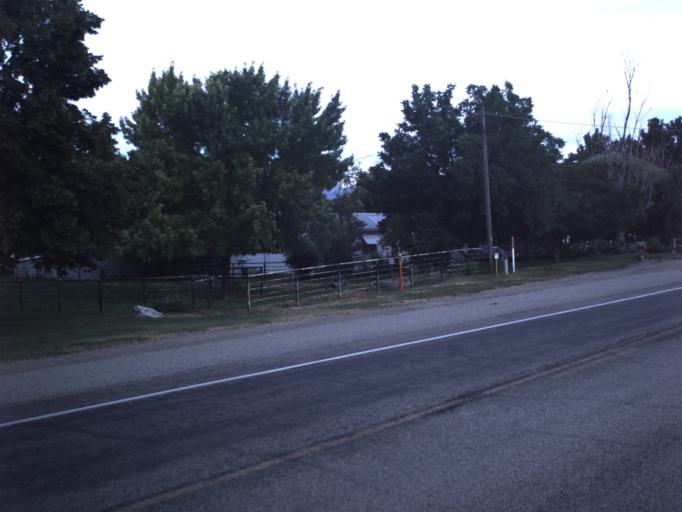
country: US
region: Utah
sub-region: Weber County
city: Farr West
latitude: 41.2872
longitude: -112.0280
